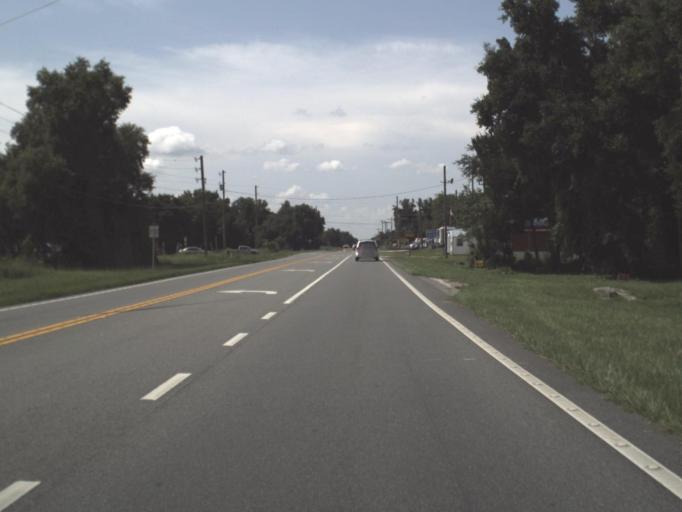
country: US
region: Florida
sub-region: Citrus County
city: Inverness Highlands North
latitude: 28.8765
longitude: -82.3630
